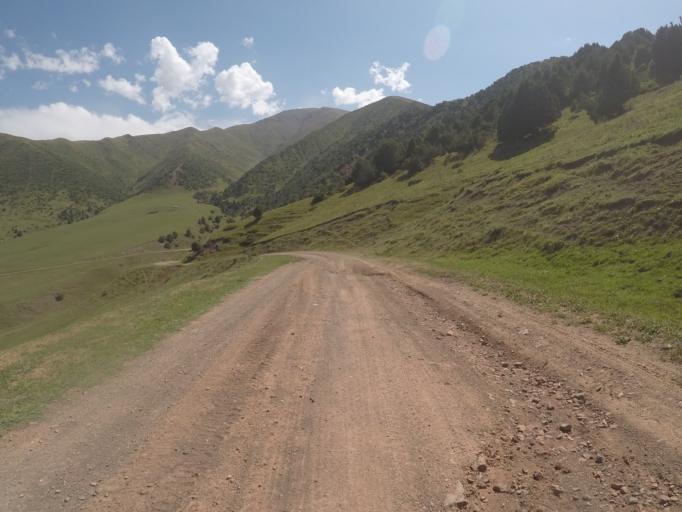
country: KG
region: Chuy
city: Bishkek
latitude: 42.6461
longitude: 74.5693
